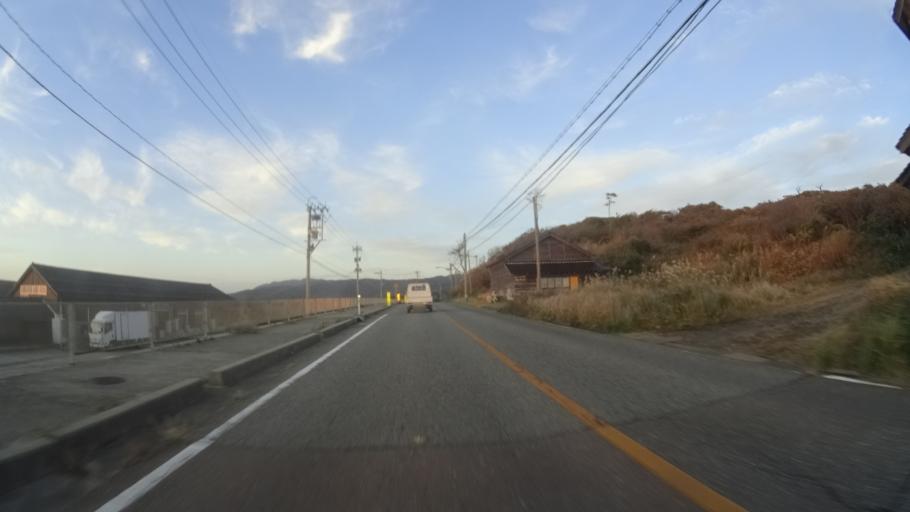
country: JP
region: Ishikawa
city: Nanao
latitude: 37.2738
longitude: 136.7321
